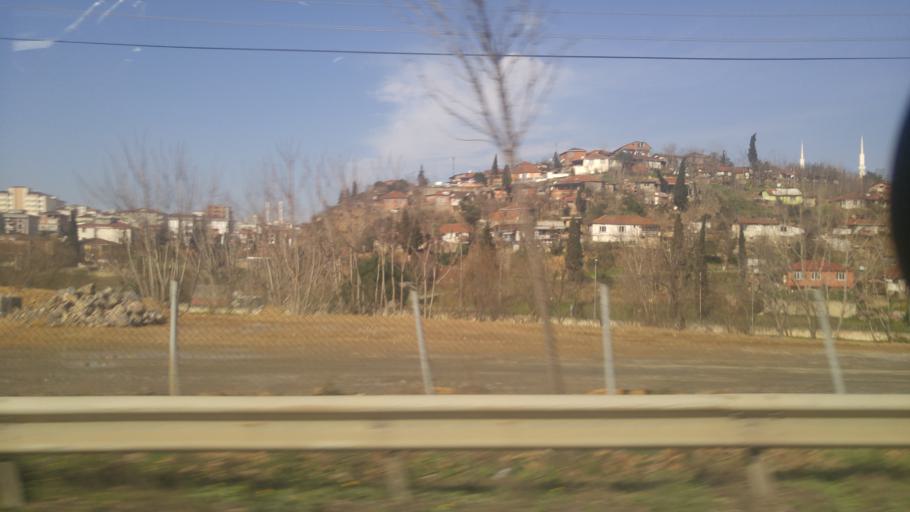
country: TR
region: Kocaeli
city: Darica
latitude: 40.8326
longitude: 29.3692
